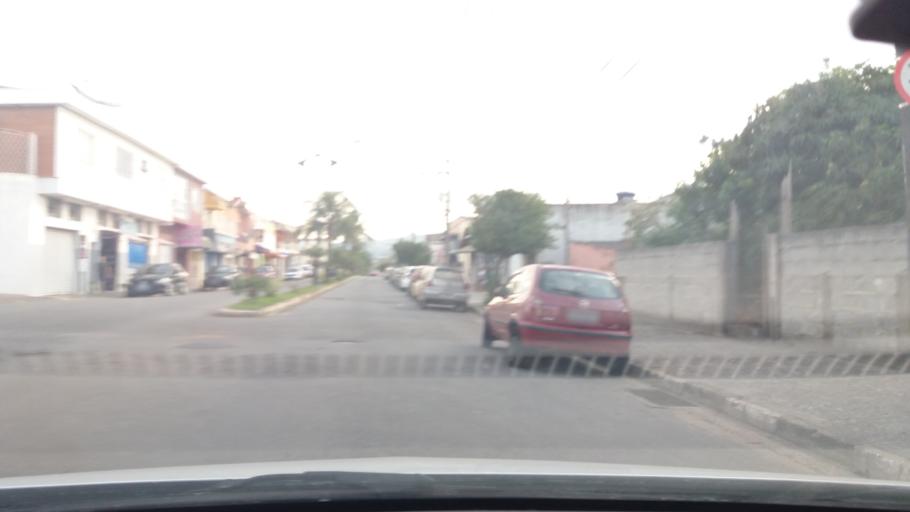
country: BR
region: Sao Paulo
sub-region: Bom Jesus Dos Perdoes
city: Bom Jesus dos Perdoes
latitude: -23.1381
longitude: -46.4665
